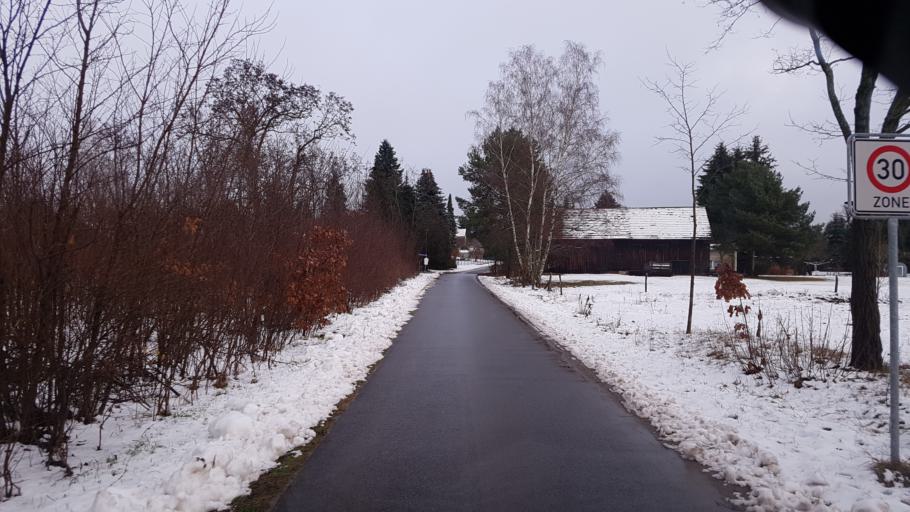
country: DE
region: Brandenburg
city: Straupitz
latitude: 51.9768
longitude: 14.1859
